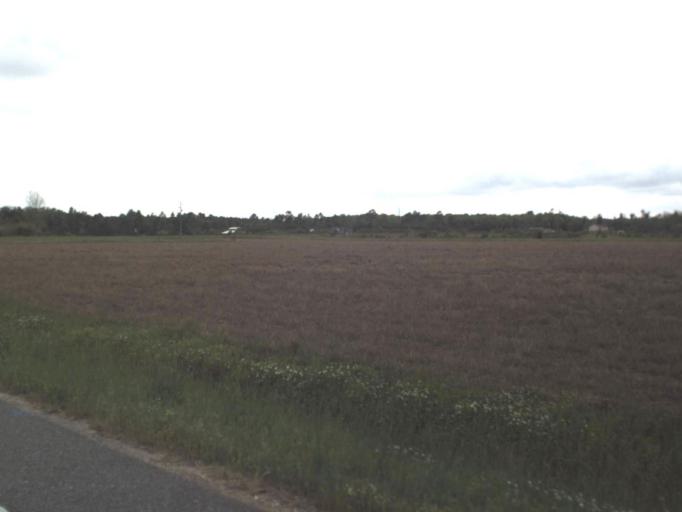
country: US
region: Florida
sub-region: Santa Rosa County
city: Point Baker
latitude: 30.7654
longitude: -87.0422
